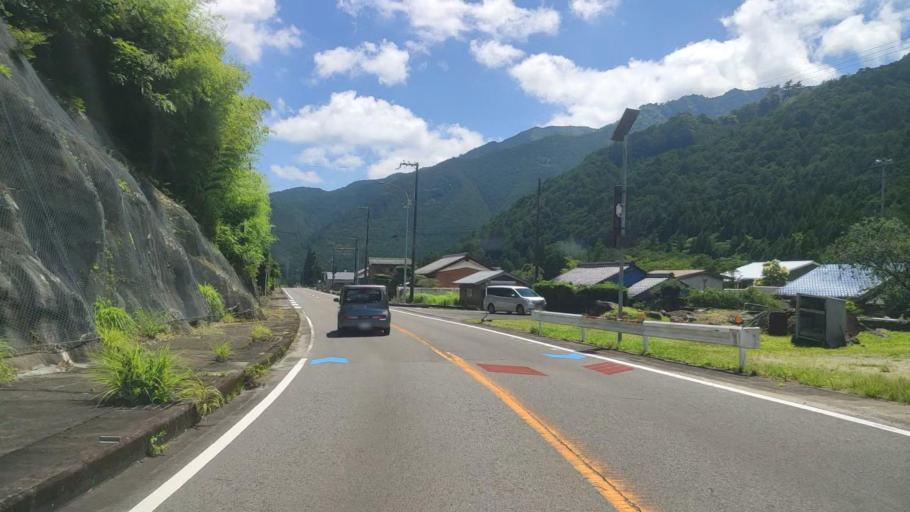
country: JP
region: Mie
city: Owase
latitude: 33.9802
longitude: 136.1050
